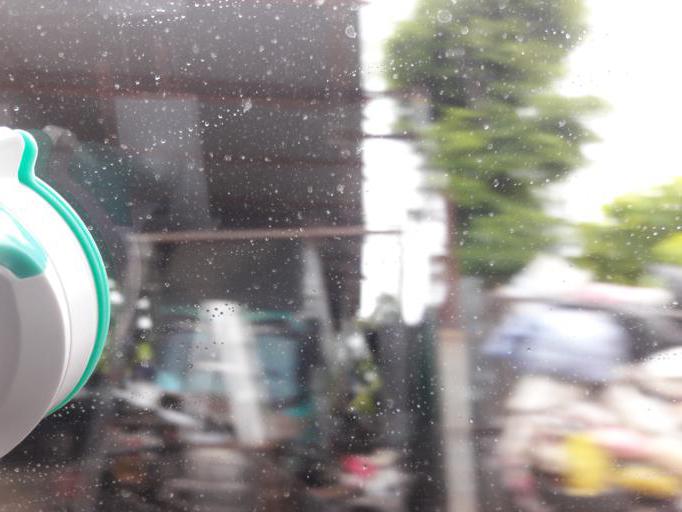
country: TH
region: Ratchaburi
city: Damnoen Saduak
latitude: 13.5274
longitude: 99.9726
